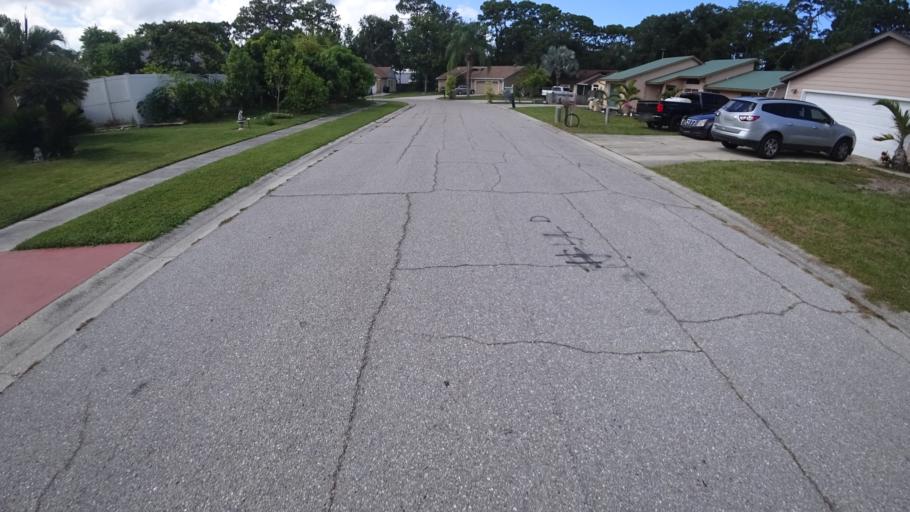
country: US
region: Florida
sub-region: Manatee County
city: Samoset
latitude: 27.4409
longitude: -82.5379
